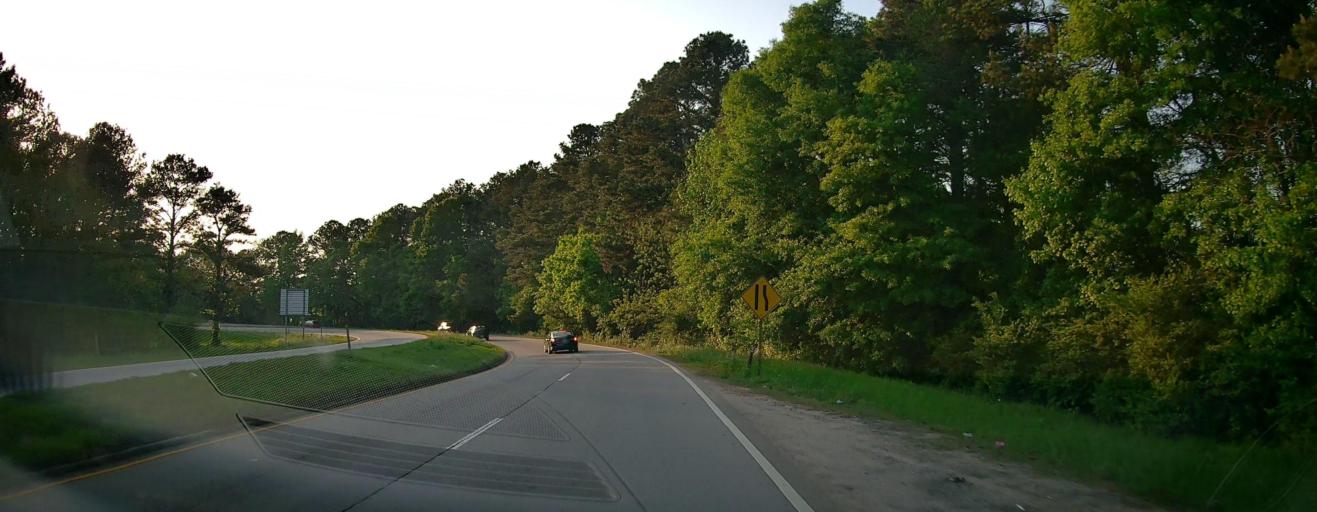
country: US
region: Georgia
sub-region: Newton County
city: Oxford
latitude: 33.6080
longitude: -83.8761
